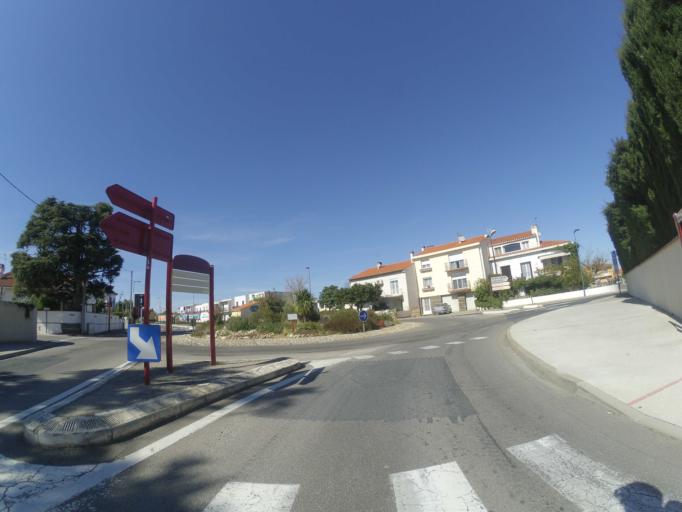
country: FR
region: Languedoc-Roussillon
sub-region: Departement des Pyrenees-Orientales
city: Toulouges
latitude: 42.6725
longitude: 2.8282
